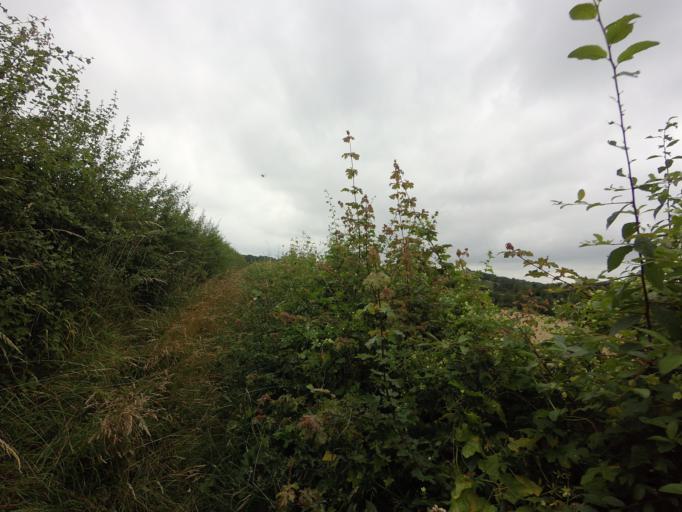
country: NL
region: Limburg
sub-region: Gemeente Maastricht
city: Heer
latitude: 50.8166
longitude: 5.7709
